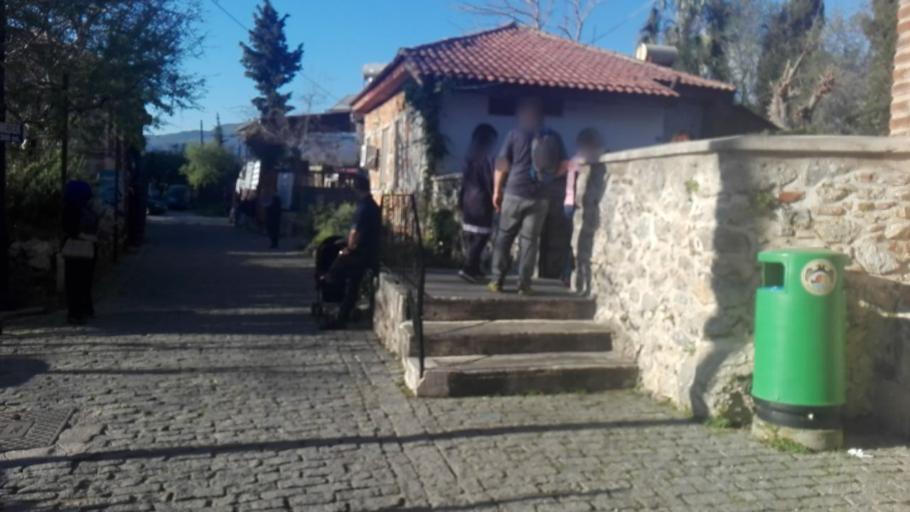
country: TR
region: Antalya
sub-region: Alanya
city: Alanya
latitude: 36.5349
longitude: 31.9927
